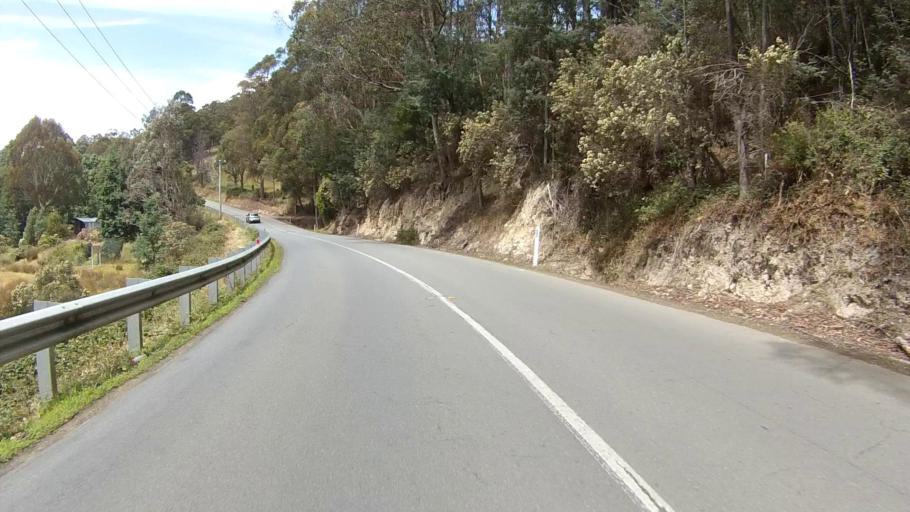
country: AU
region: Tasmania
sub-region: Kingborough
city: Kettering
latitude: -43.1041
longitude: 147.2164
